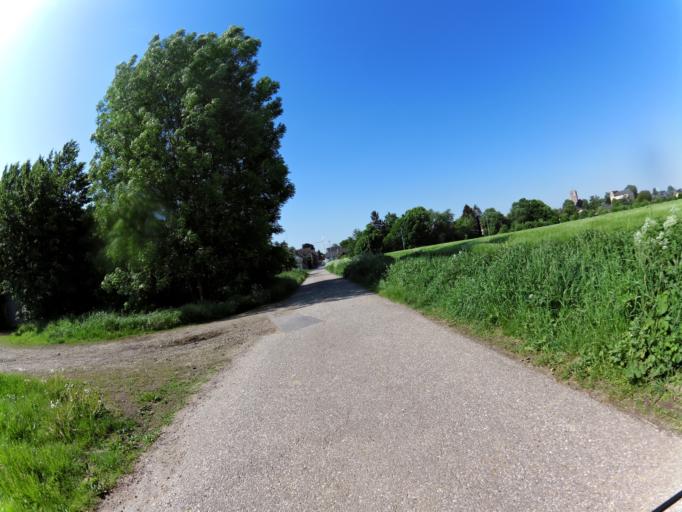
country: DE
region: North Rhine-Westphalia
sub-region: Regierungsbezirk Koln
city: Linnich
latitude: 51.0035
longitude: 6.2498
